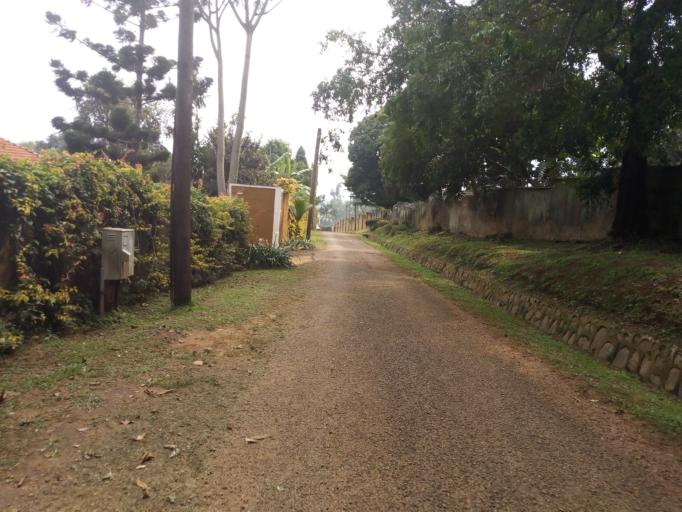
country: UG
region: Central Region
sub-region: Wakiso District
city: Kireka
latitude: 0.3231
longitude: 32.6257
